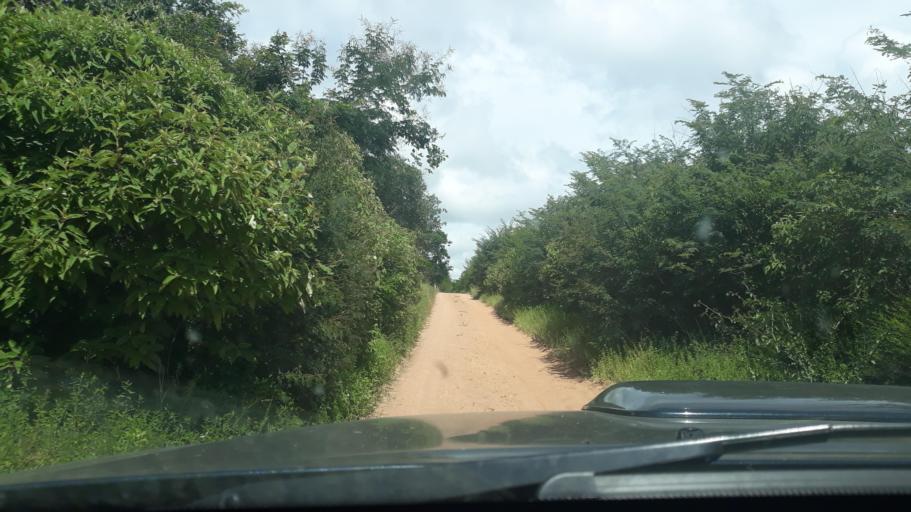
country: BR
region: Bahia
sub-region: Riacho De Santana
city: Riacho de Santana
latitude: -13.8589
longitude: -43.0381
